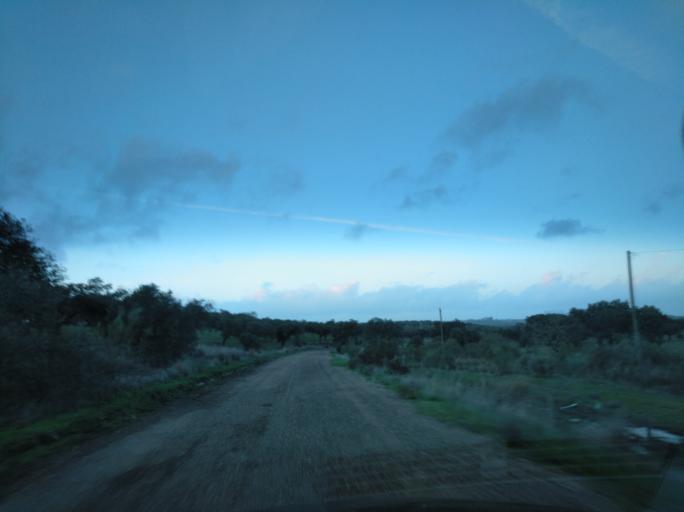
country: PT
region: Portalegre
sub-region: Campo Maior
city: Campo Maior
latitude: 39.0850
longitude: -7.1175
